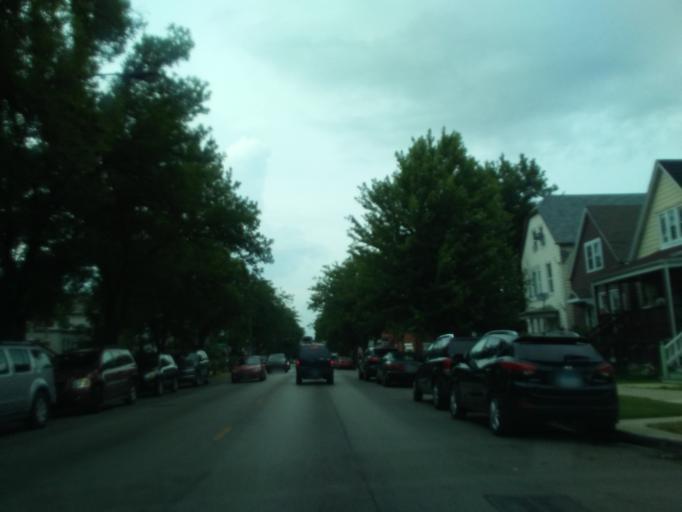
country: US
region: Illinois
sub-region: Cook County
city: Oak Park
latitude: 41.9193
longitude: -87.7364
